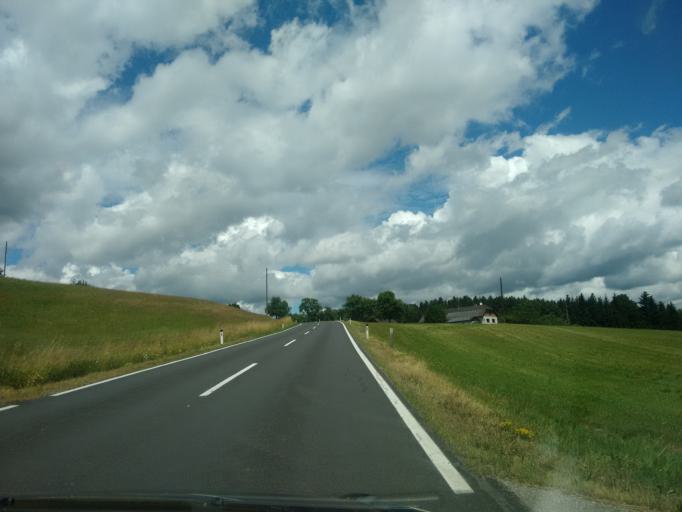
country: AT
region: Upper Austria
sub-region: Politischer Bezirk Urfahr-Umgebung
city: Gramastetten
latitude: 48.3876
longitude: 14.1913
